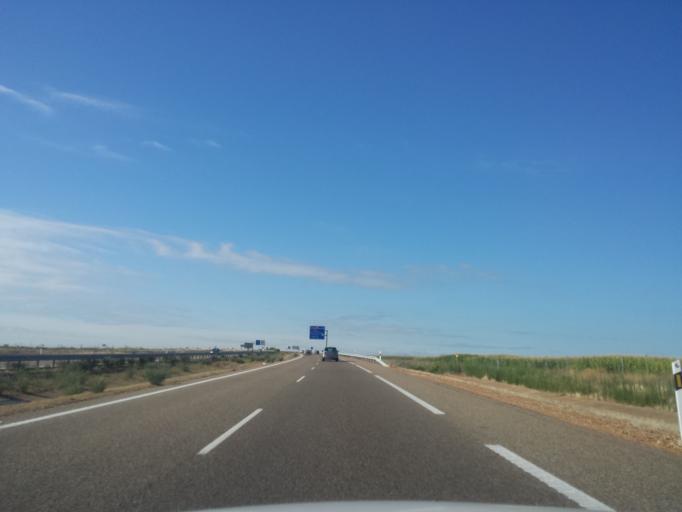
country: ES
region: Castille and Leon
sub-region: Provincia de Leon
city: Villamanan
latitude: 42.3381
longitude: -5.6083
